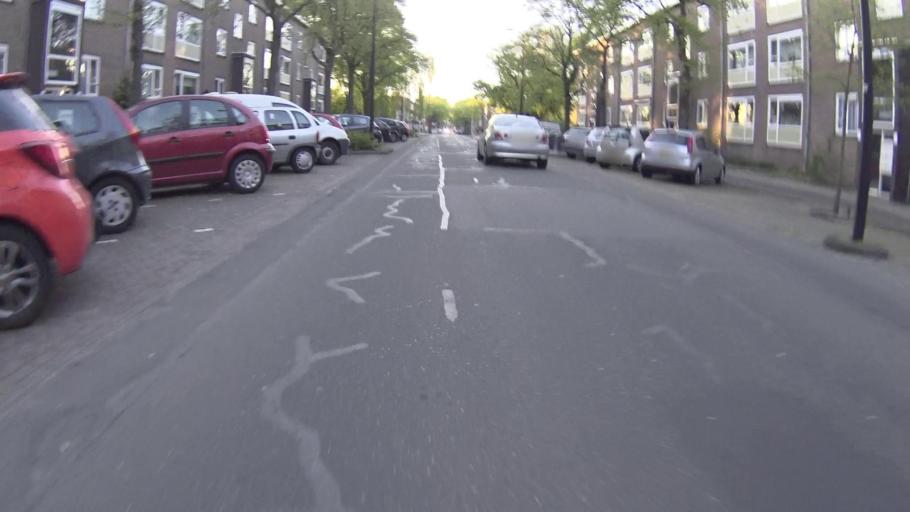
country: NL
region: South Holland
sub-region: Gemeente Rijswijk
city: Rijswijk
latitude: 52.0566
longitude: 4.3310
